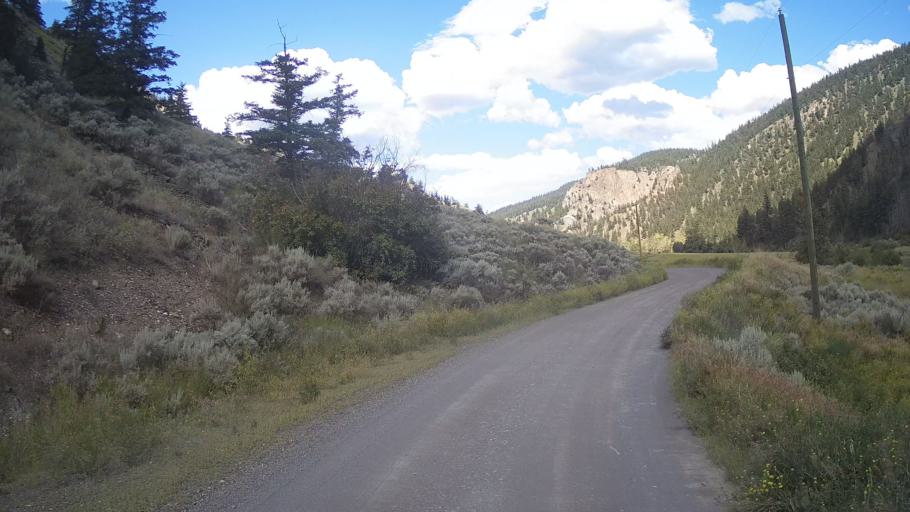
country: CA
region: British Columbia
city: Lillooet
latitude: 51.2215
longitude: -122.0745
